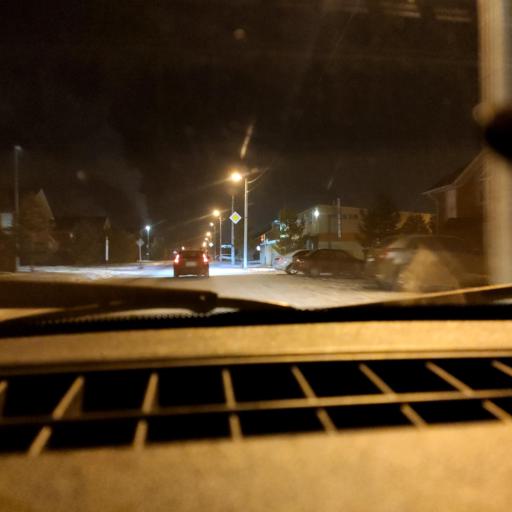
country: RU
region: Bashkortostan
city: Ufa
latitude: 54.5977
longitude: 55.9223
